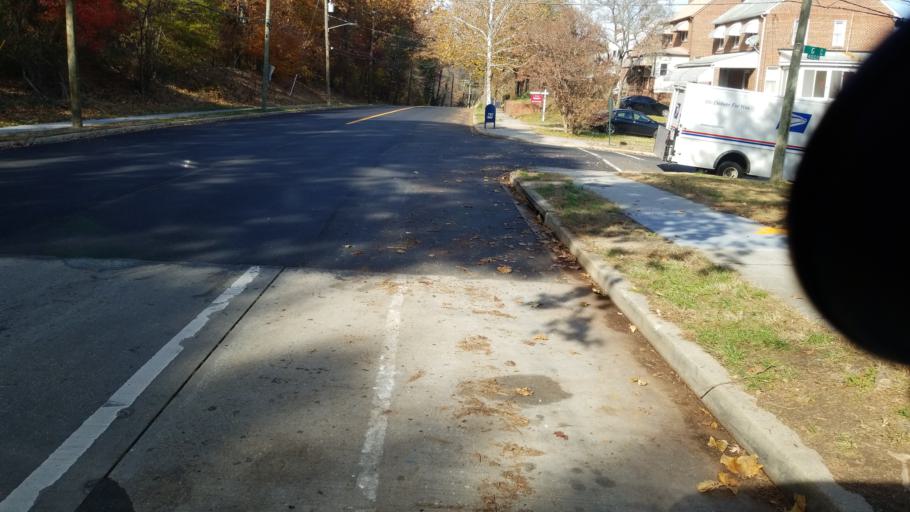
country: US
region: Maryland
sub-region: Prince George's County
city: Coral Hills
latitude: 38.8789
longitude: -76.9446
